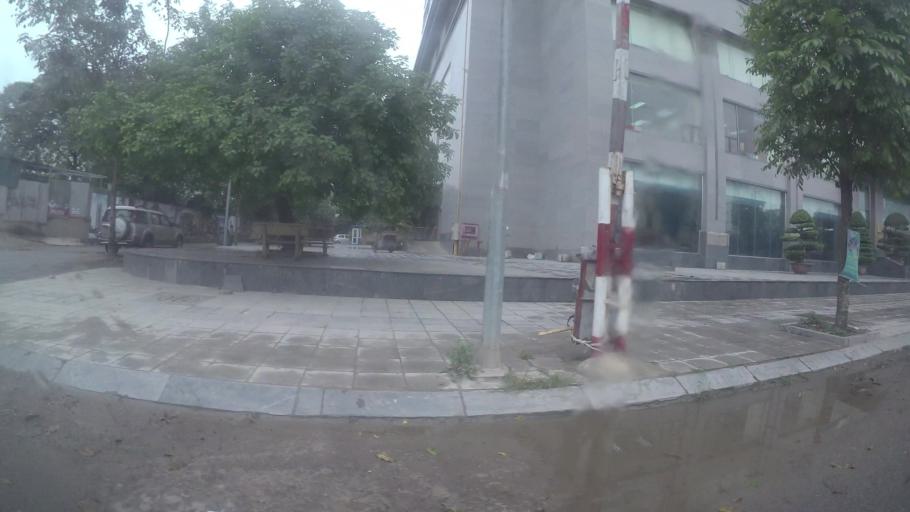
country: VN
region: Ha Noi
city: Cau Giay
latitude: 21.0225
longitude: 105.7864
